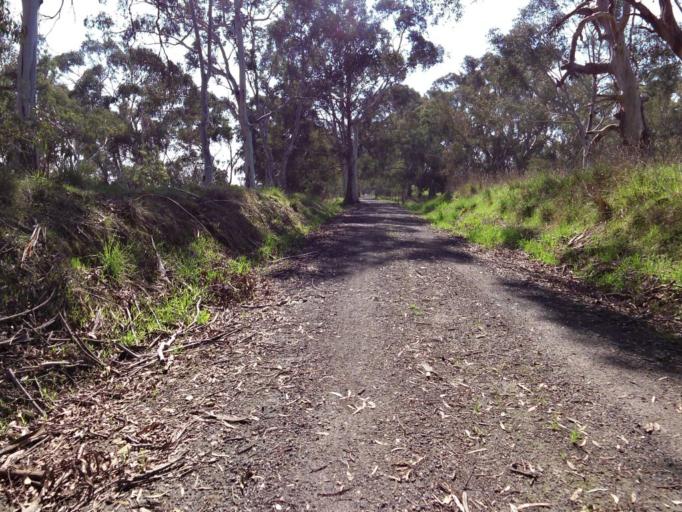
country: AU
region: Victoria
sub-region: Murrindindi
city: Alexandra
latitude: -37.1199
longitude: 145.6031
